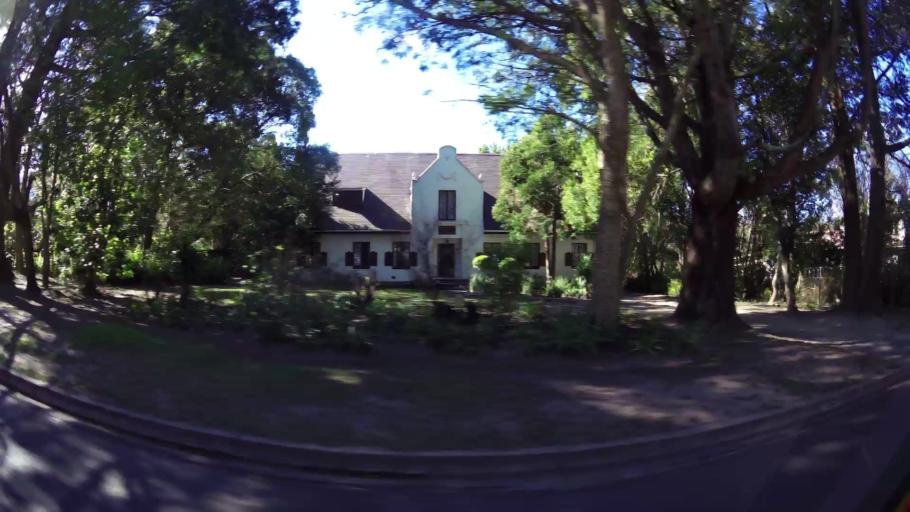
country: ZA
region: Western Cape
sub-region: Eden District Municipality
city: George
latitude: -33.9502
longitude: 22.4442
